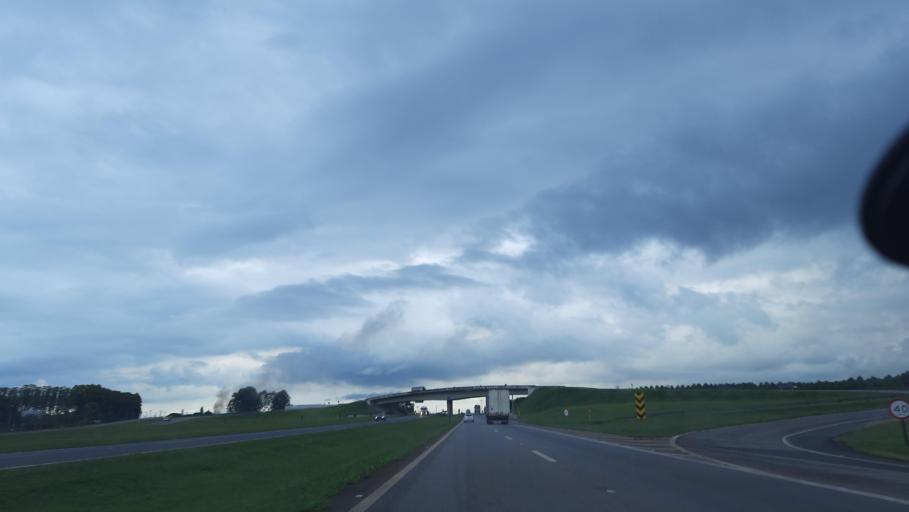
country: BR
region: Sao Paulo
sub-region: Moji-Guacu
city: Mogi-Gaucu
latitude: -22.3183
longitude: -46.9635
